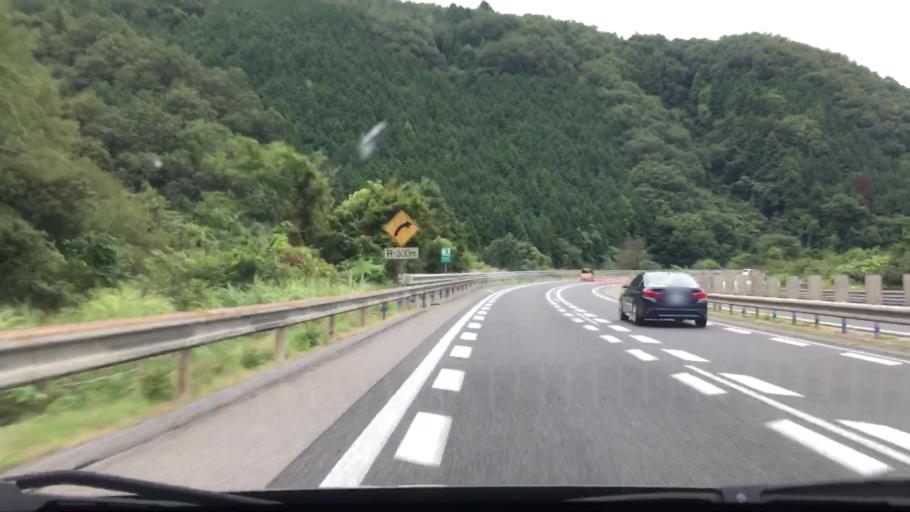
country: JP
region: Hiroshima
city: Miyoshi
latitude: 34.7819
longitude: 132.8439
